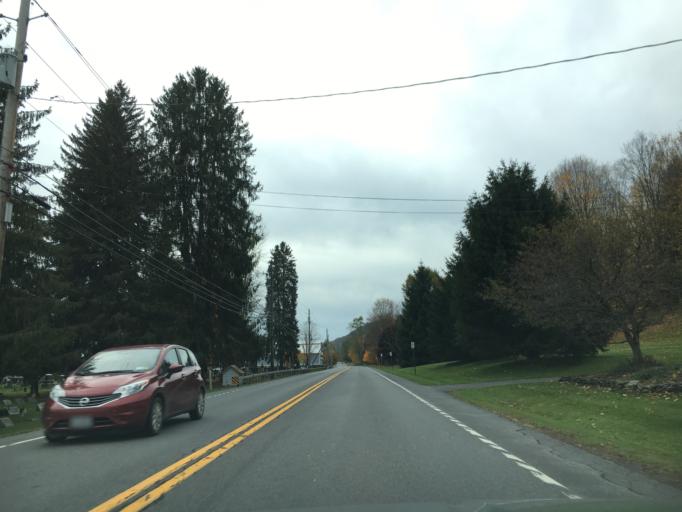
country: US
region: New York
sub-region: Otsego County
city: Cooperstown
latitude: 42.6480
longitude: -74.9647
